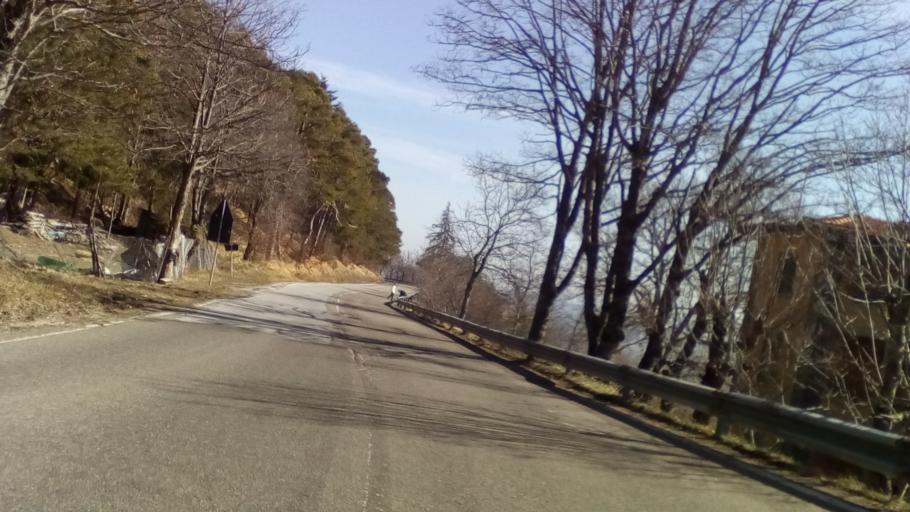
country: IT
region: Emilia-Romagna
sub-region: Provincia di Modena
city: Riolunato
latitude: 44.2715
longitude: 10.6773
